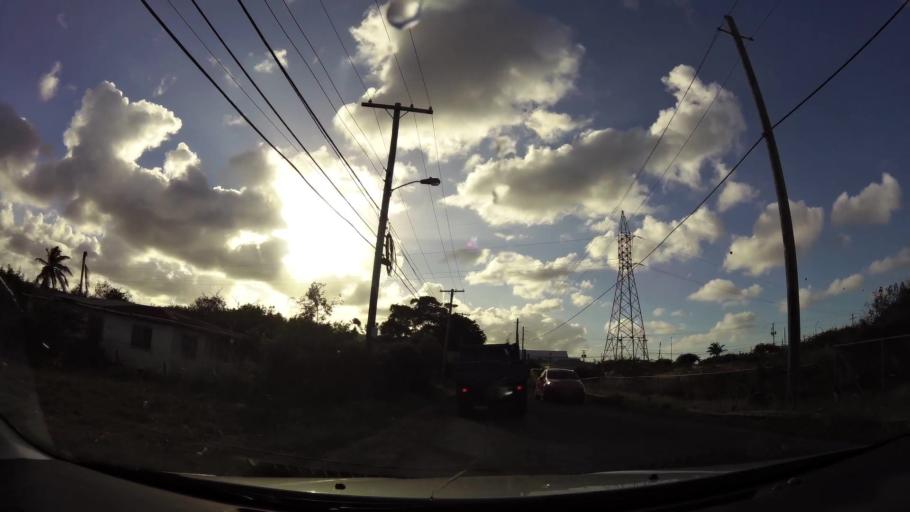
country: AG
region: Saint George
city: Piggotts
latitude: 17.1263
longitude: -61.8119
